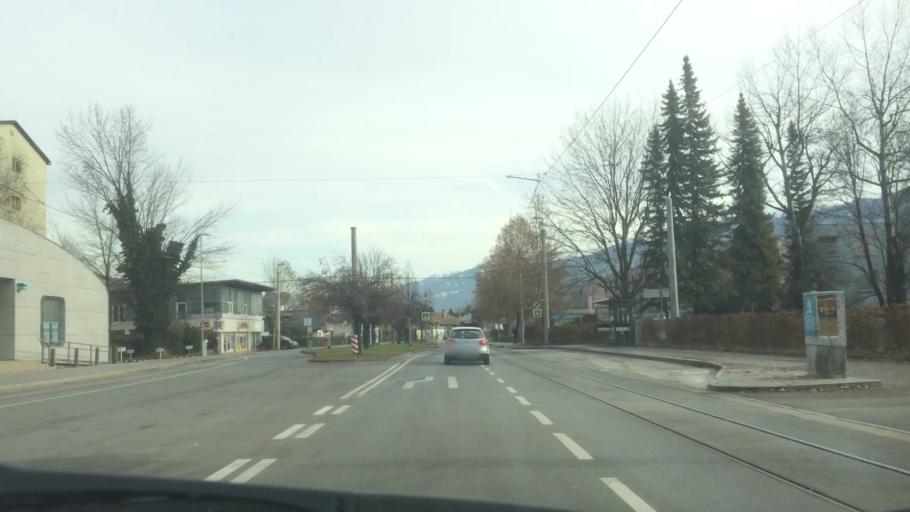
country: AT
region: Tyrol
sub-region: Politischer Bezirk Innsbruck Land
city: Vols
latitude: 47.2652
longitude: 11.3469
